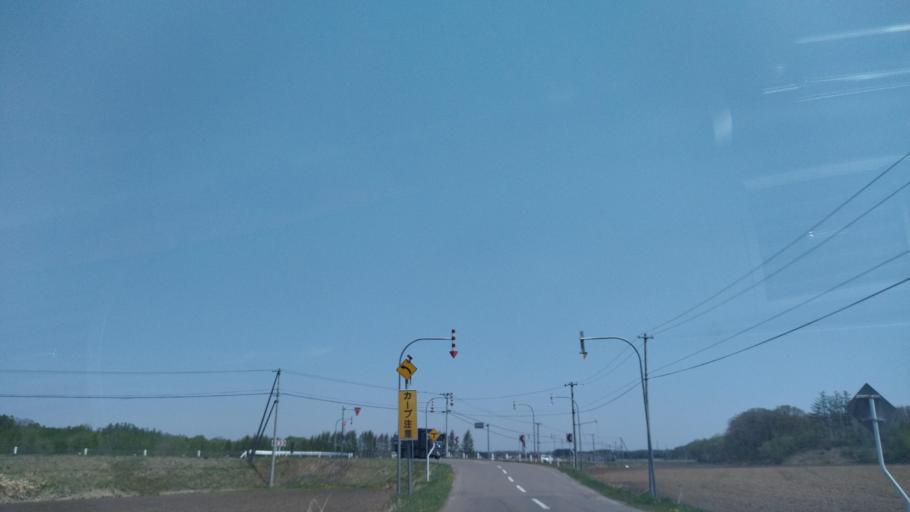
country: JP
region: Hokkaido
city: Obihiro
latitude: 42.9018
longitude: 143.0113
